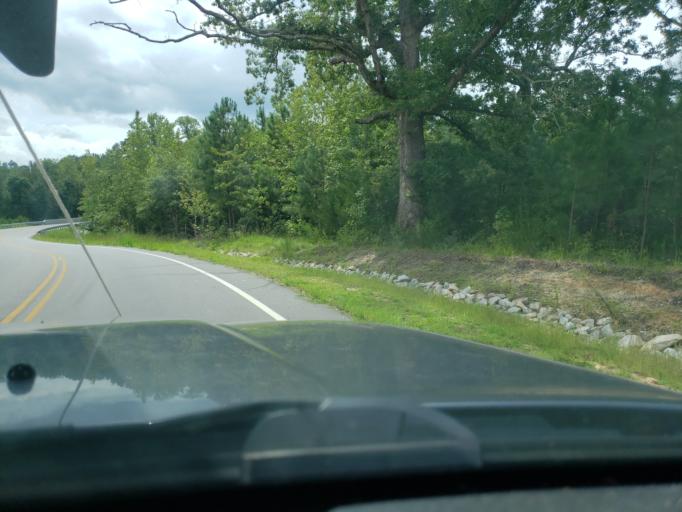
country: US
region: North Carolina
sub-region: Wake County
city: Zebulon
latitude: 35.9006
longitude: -78.3315
